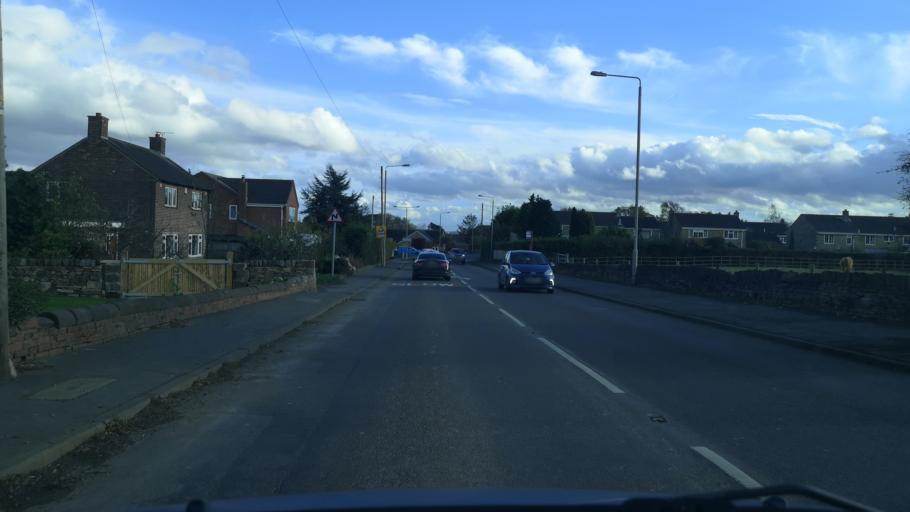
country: GB
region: England
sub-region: City and Borough of Wakefield
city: Horbury
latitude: 53.6213
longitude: -1.5694
